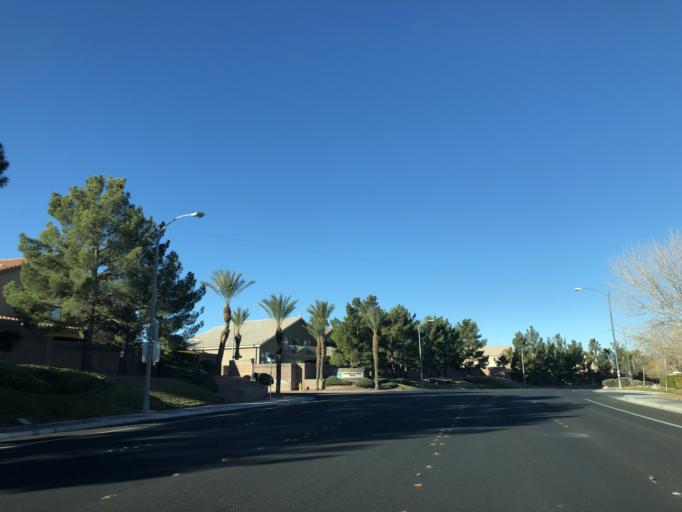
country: US
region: Nevada
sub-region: Clark County
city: Whitney
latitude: 36.0180
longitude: -115.0488
